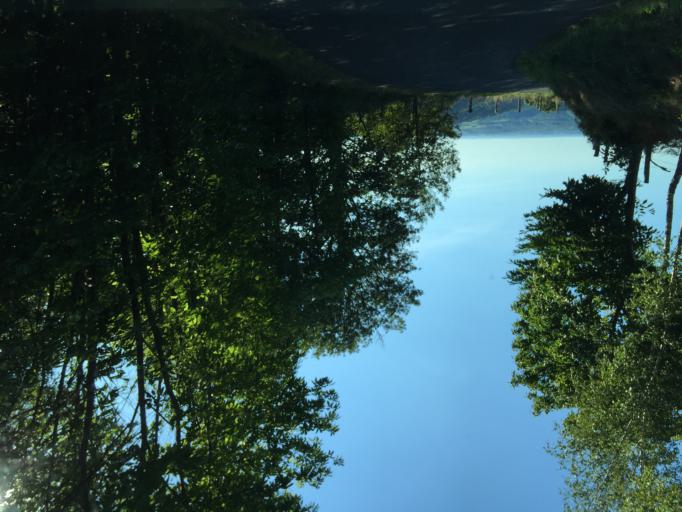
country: FR
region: Midi-Pyrenees
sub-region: Departement de l'Aveyron
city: Espalion
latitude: 44.5863
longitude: 2.6915
